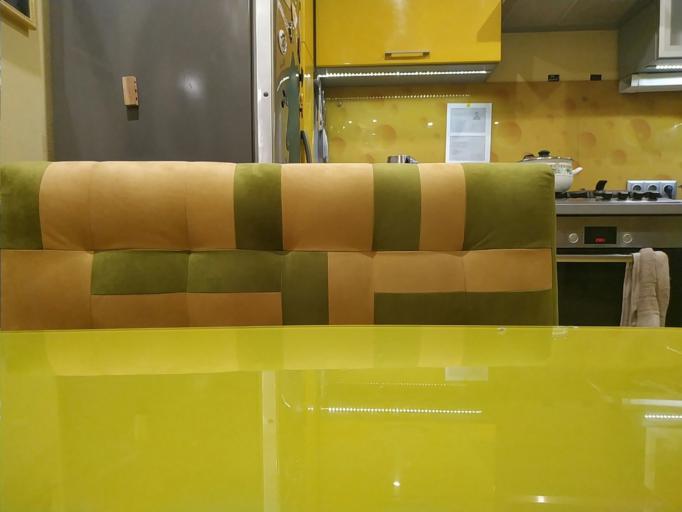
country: RU
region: Murmansk
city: Alakurtti
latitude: 66.1365
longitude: 30.3192
